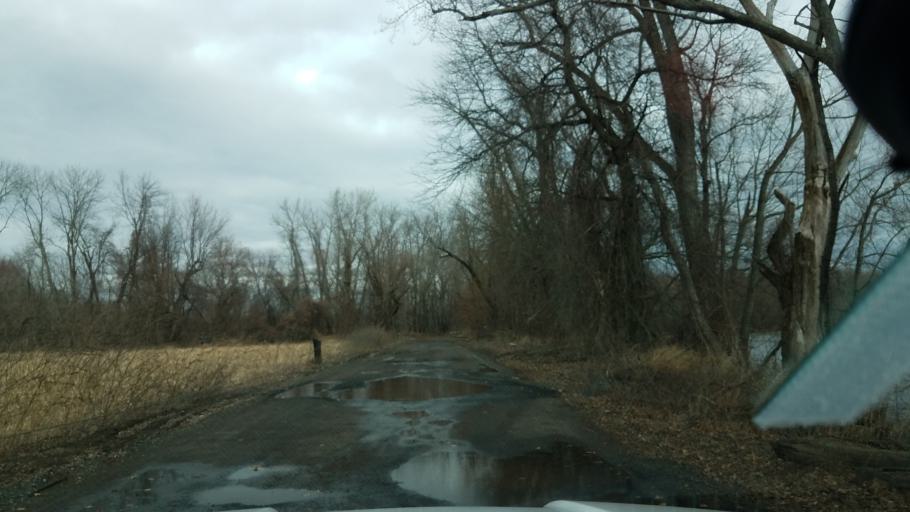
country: US
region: Connecticut
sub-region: Hartford County
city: Wethersfield
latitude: 41.6979
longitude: -72.6377
